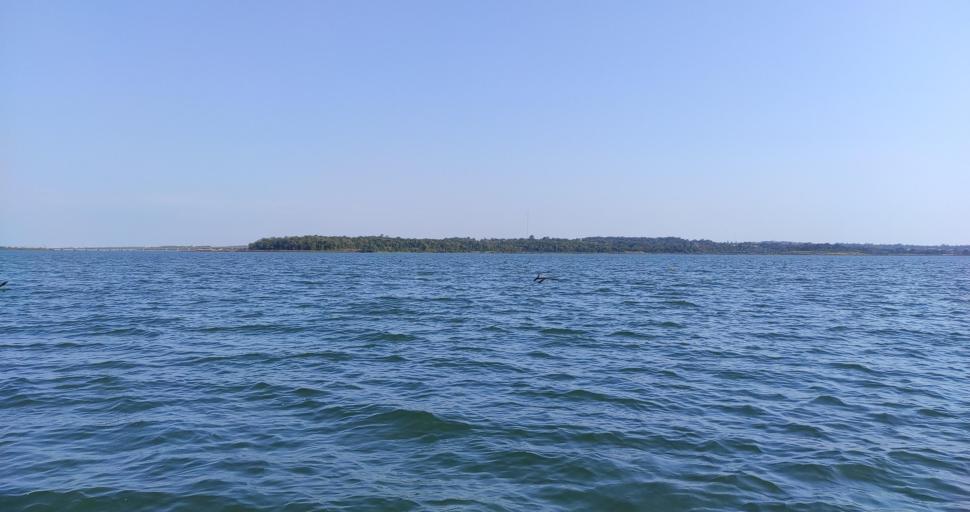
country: AR
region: Misiones
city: Garupa
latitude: -27.4440
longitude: -55.8079
